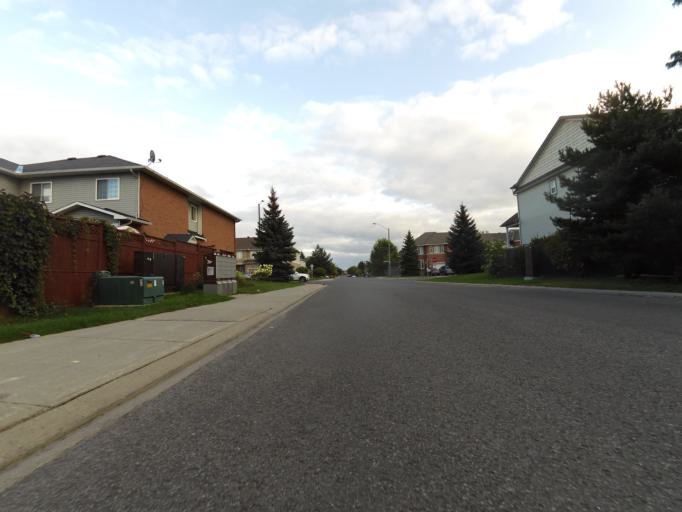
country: CA
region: Ontario
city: Bells Corners
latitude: 45.2816
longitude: -75.7328
